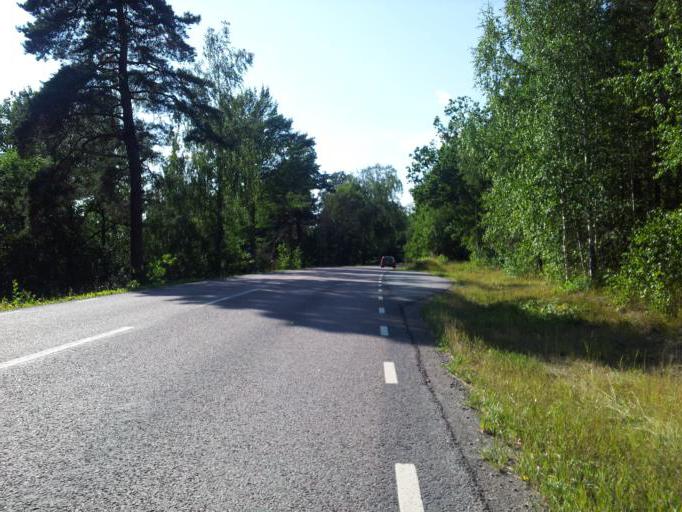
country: SE
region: Uppsala
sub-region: Knivsta Kommun
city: Knivsta
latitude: 59.8797
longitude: 17.9999
